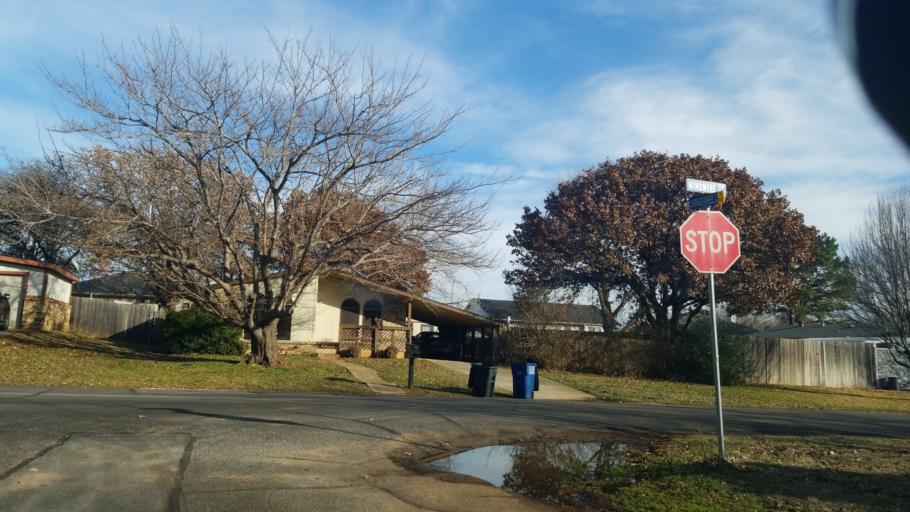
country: US
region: Texas
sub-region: Denton County
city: Corinth
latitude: 33.1383
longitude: -97.0609
